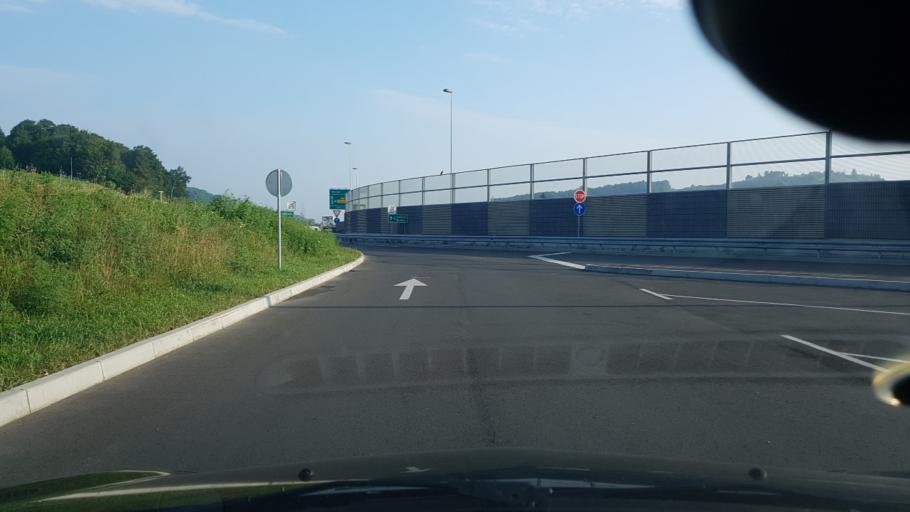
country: SI
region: Podlehnik
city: Podlehnik
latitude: 46.3284
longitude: 15.8795
